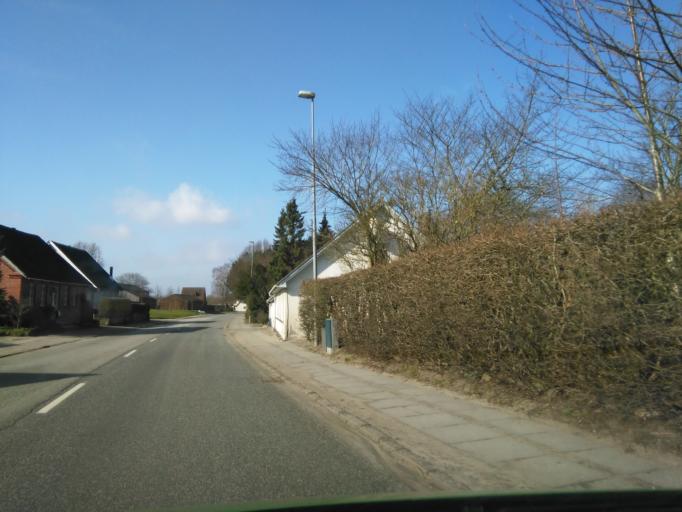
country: DK
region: Central Jutland
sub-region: Arhus Kommune
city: Tranbjerg
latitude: 56.1046
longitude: 10.1430
